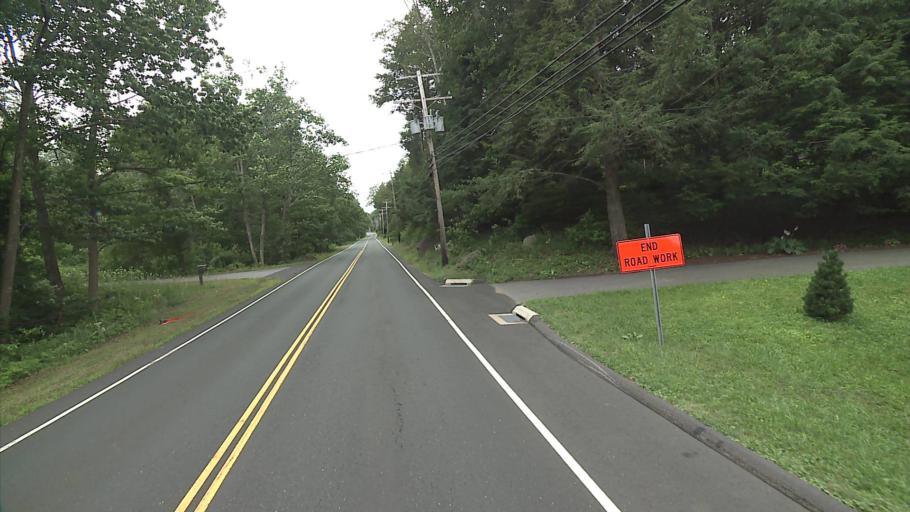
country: US
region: Connecticut
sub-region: Litchfield County
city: Winsted
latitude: 41.9923
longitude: -73.0465
